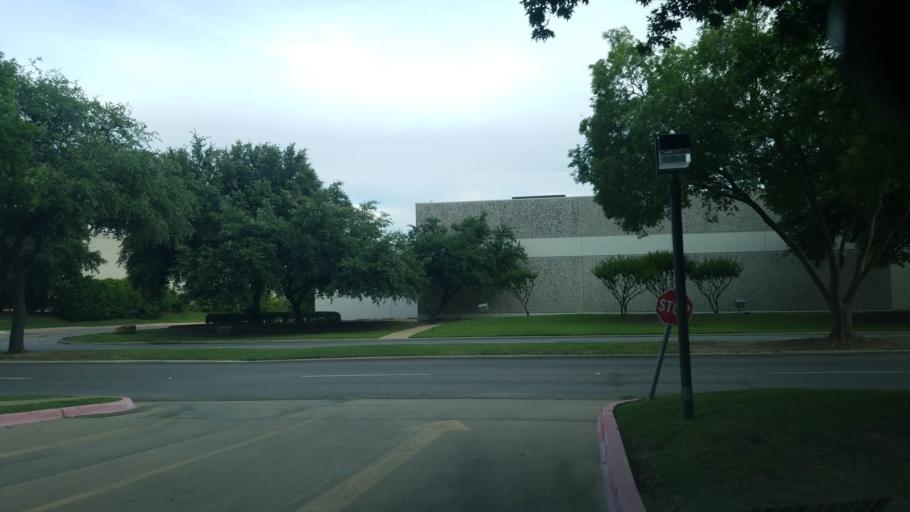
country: US
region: Texas
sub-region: Dallas County
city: Irving
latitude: 32.8716
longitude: -96.9873
